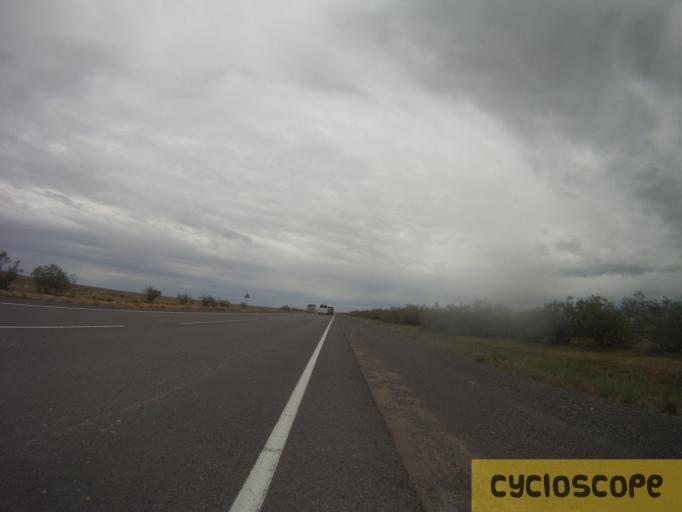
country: KG
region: Chuy
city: Ivanovka
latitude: 43.3983
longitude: 75.1202
